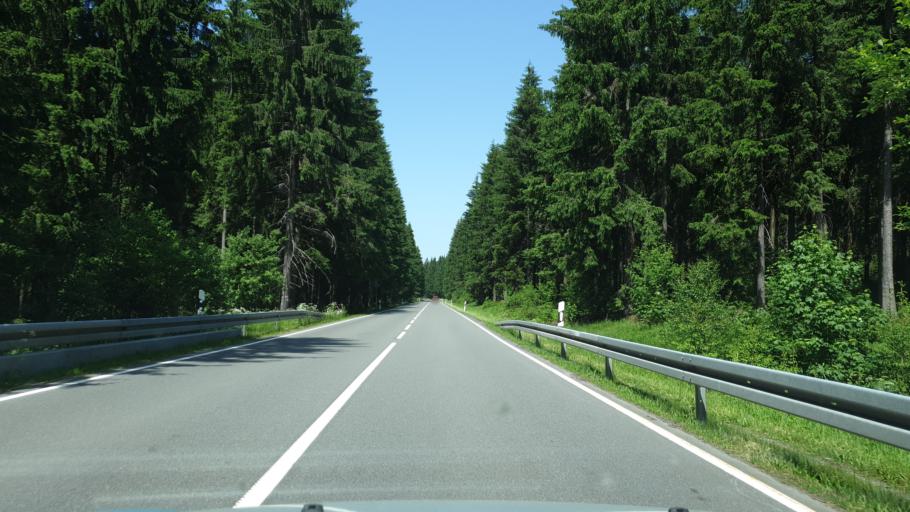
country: DE
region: Saxony
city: Hammerbrucke
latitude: 50.4031
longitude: 12.4237
